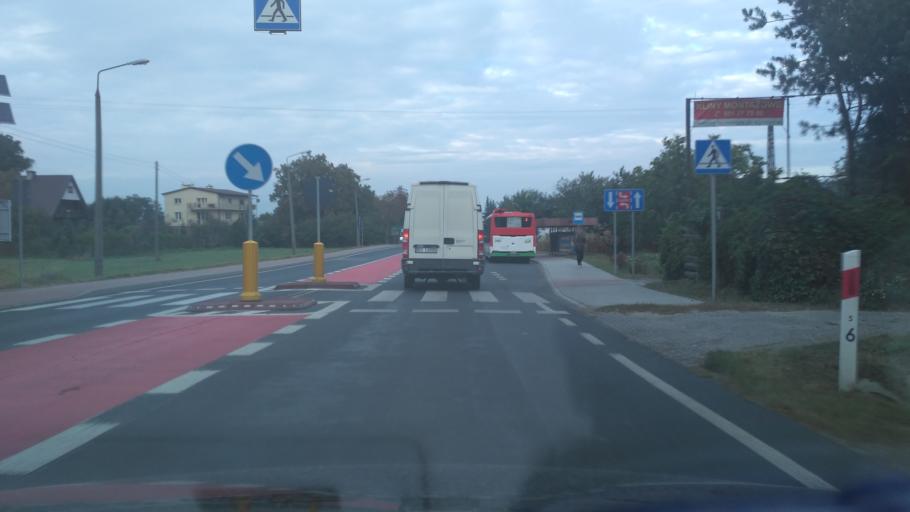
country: PL
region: Lublin Voivodeship
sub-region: Powiat lubelski
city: Jakubowice Murowane
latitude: 51.2705
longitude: 22.6398
